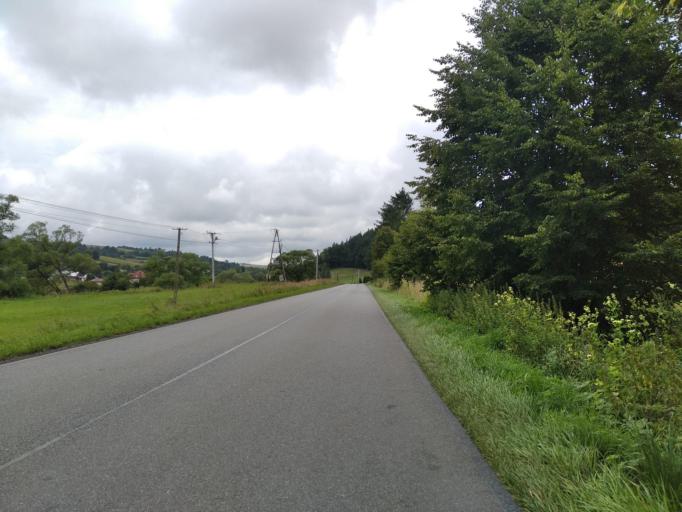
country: PL
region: Subcarpathian Voivodeship
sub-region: Powiat przemyski
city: Bircza
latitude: 49.6924
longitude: 22.3908
